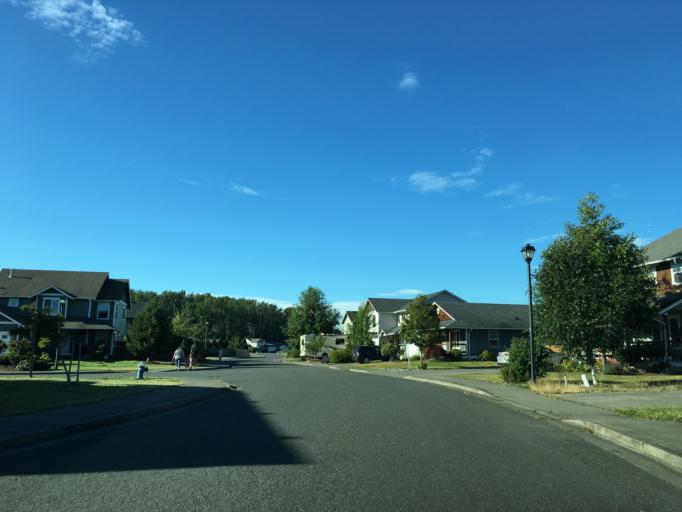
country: US
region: Washington
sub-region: Whatcom County
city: Birch Bay
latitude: 48.9091
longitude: -122.7438
